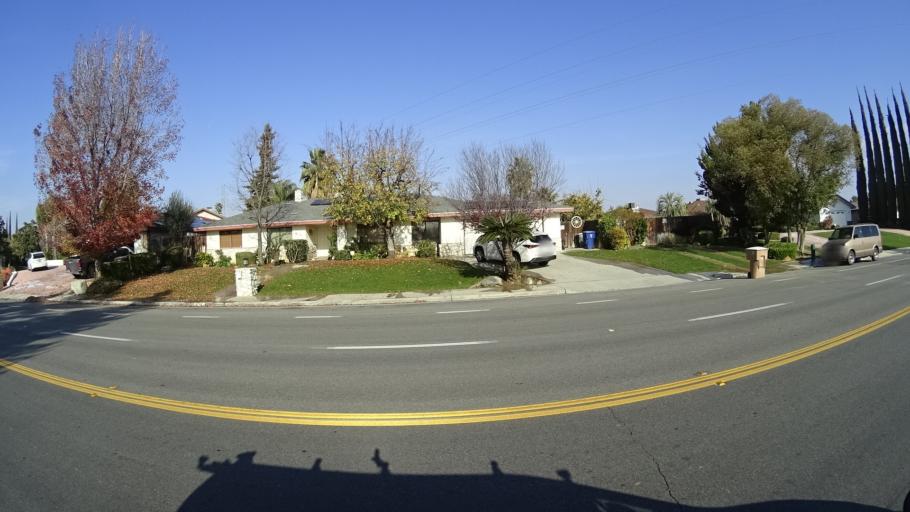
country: US
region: California
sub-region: Kern County
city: Oildale
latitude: 35.4094
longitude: -118.9409
